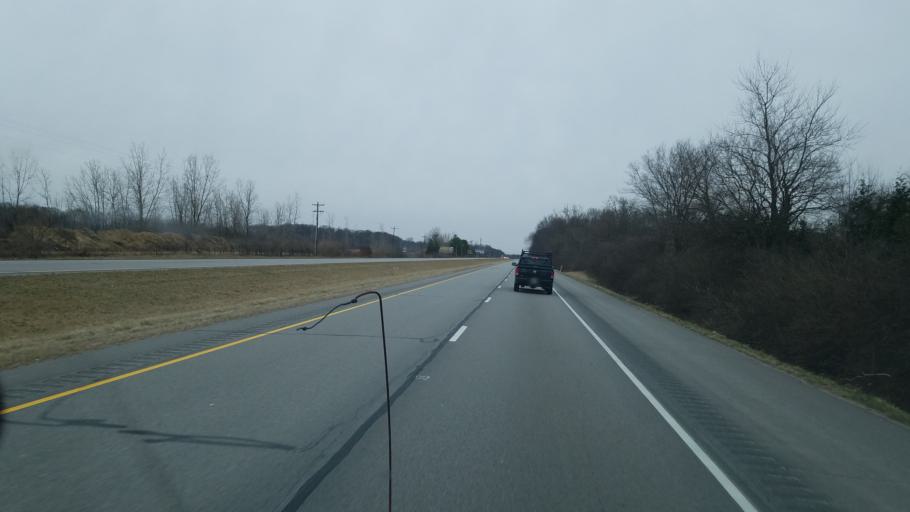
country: US
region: Indiana
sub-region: Marshall County
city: Plymouth
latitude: 41.3153
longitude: -86.2757
